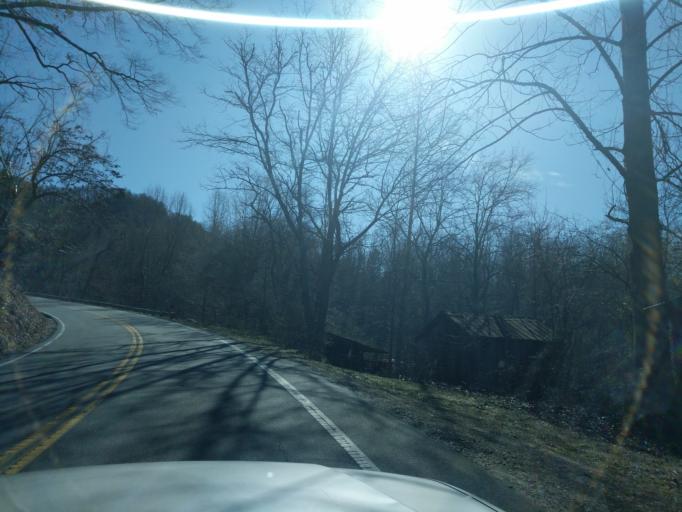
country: US
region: North Carolina
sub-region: Swain County
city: Bryson City
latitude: 35.3601
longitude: -83.5538
